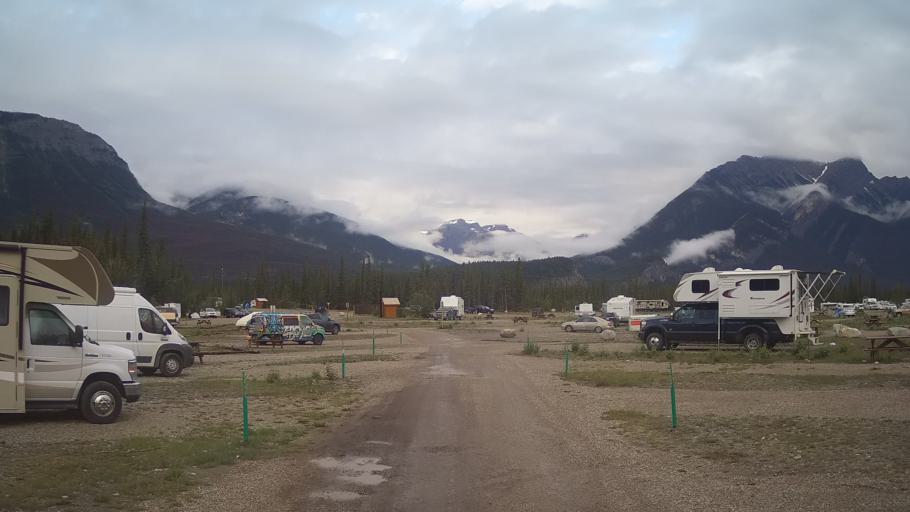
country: CA
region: Alberta
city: Jasper Park Lodge
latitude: 53.0154
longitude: -118.0827
